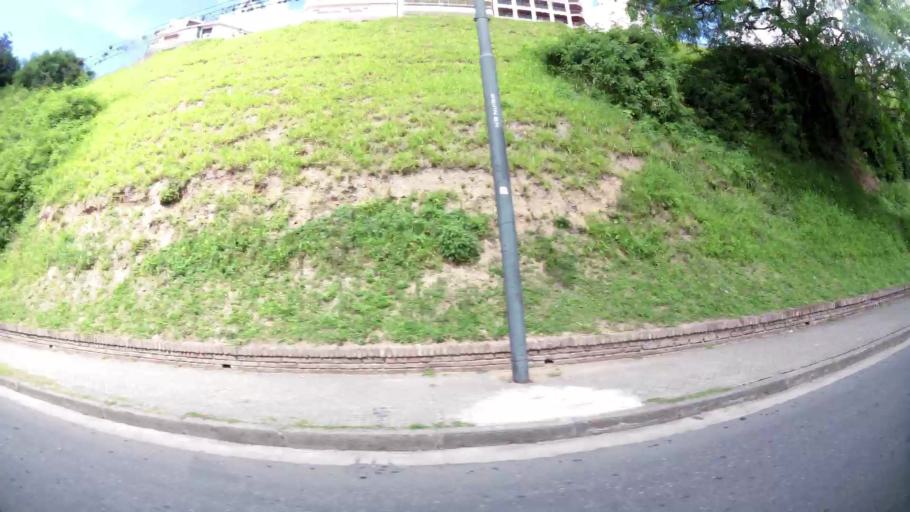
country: AR
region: Santa Fe
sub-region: Departamento de Rosario
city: Rosario
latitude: -32.9540
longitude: -60.6240
